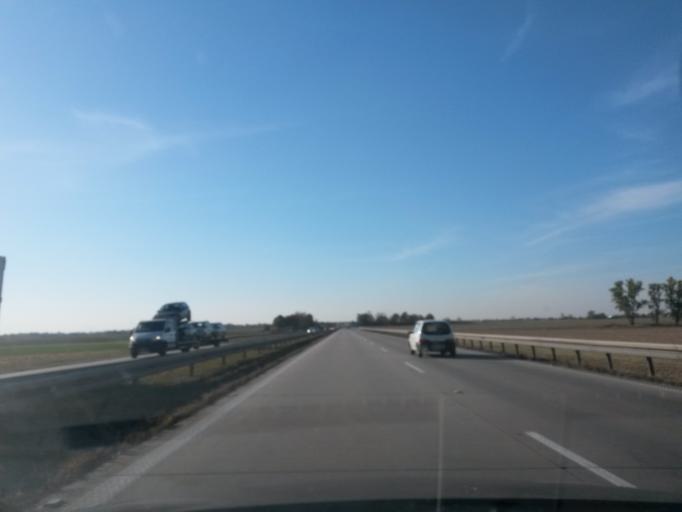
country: PL
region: Lower Silesian Voivodeship
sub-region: Powiat sredzki
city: Ciechow
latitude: 51.0555
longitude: 16.5397
